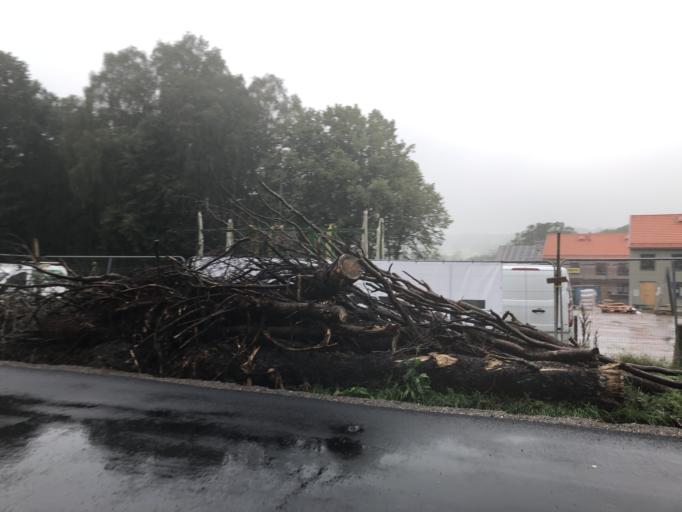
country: SE
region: Vaestra Goetaland
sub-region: Goteborg
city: Goeteborg
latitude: 57.7604
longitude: 11.9490
